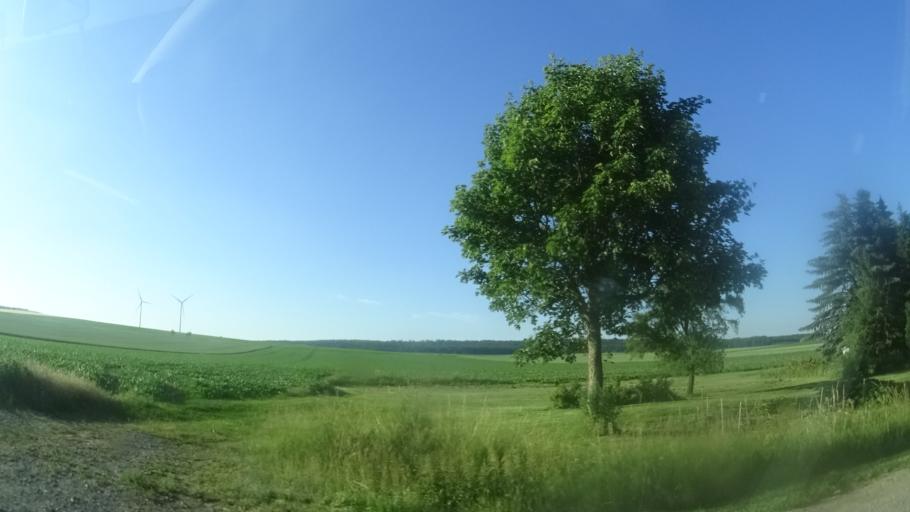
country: DE
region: Lower Saxony
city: Bad Salzdetfurth
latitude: 52.1014
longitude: 10.0647
